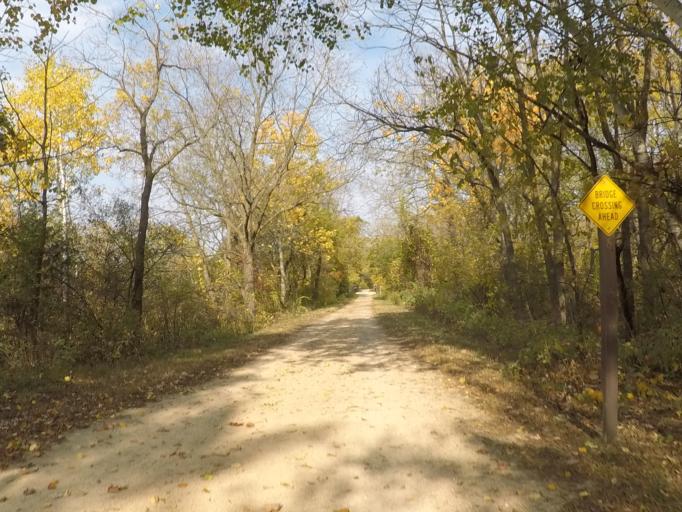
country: US
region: Wisconsin
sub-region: Iowa County
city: Barneveld
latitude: 43.0162
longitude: -89.8279
